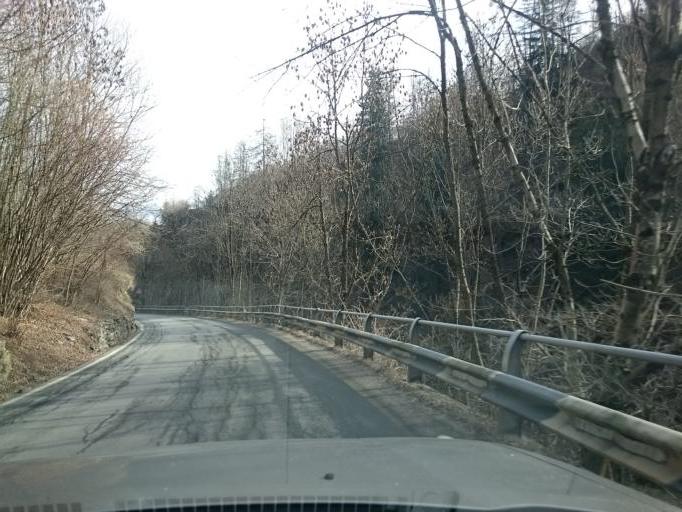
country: IT
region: Lombardy
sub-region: Provincia di Brescia
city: Corteno Golgi
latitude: 46.1655
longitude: 10.2317
